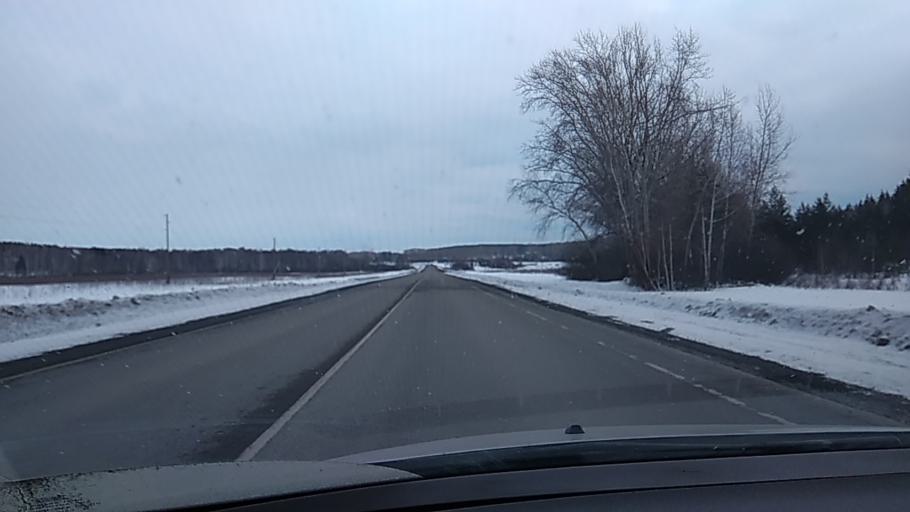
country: RU
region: Sverdlovsk
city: Dvurechensk
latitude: 56.6645
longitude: 61.1613
